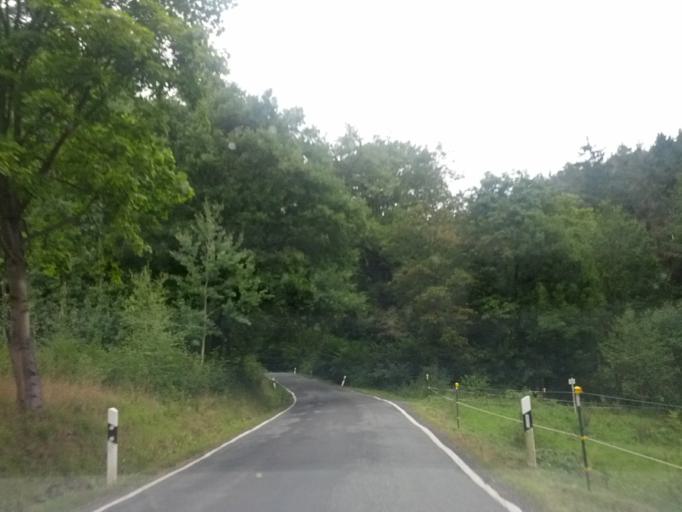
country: DE
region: Thuringia
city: Bad Salzungen
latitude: 50.8318
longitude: 10.2367
